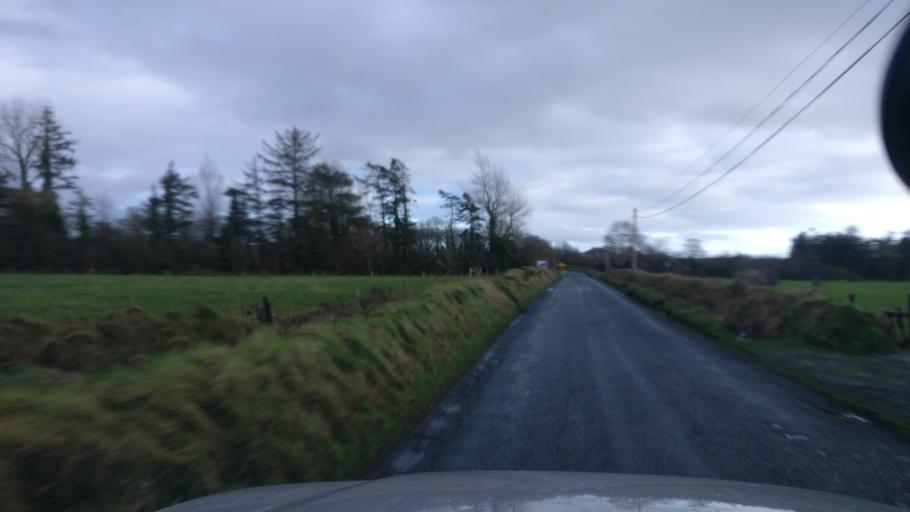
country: IE
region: Connaught
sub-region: County Galway
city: Athenry
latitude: 53.2964
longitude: -8.7002
